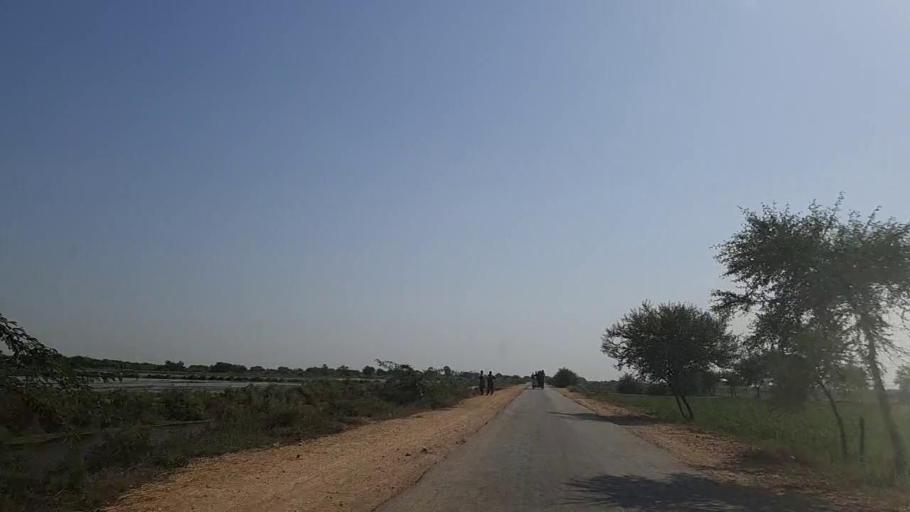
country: PK
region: Sindh
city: Mirpur Batoro
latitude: 24.6526
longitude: 68.2880
